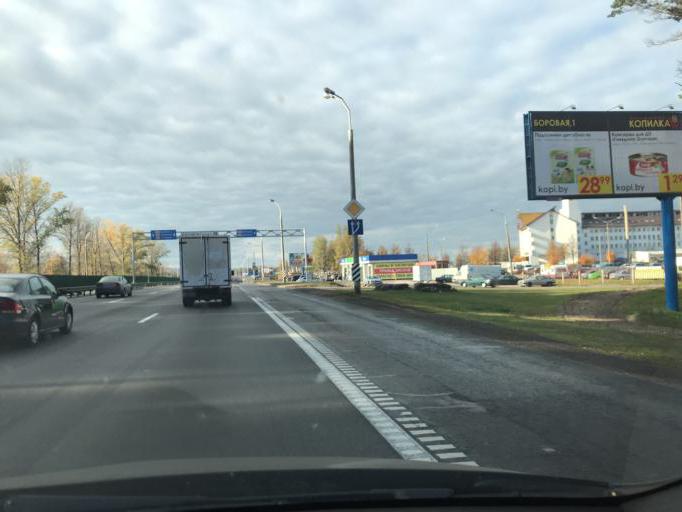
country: BY
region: Minsk
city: Borovlyany
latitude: 53.9575
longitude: 27.6338
